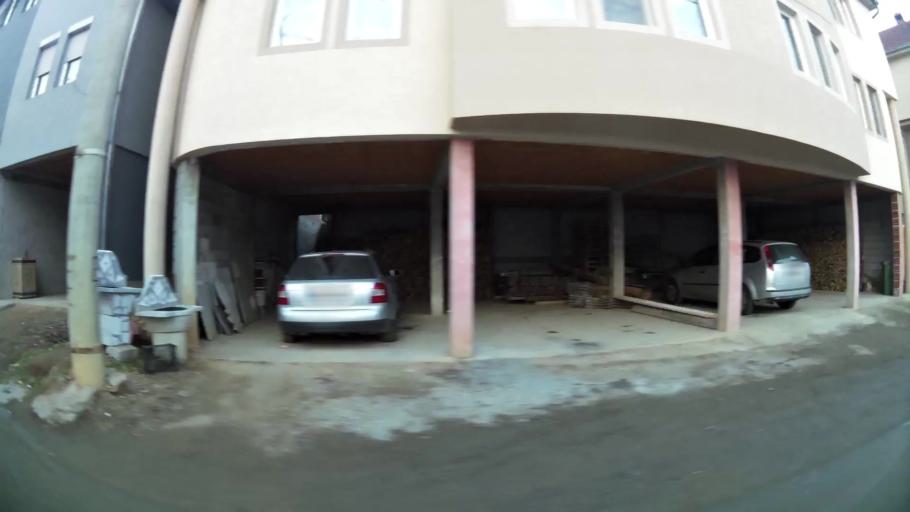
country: MK
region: Aracinovo
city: Arachinovo
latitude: 42.0282
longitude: 21.5613
